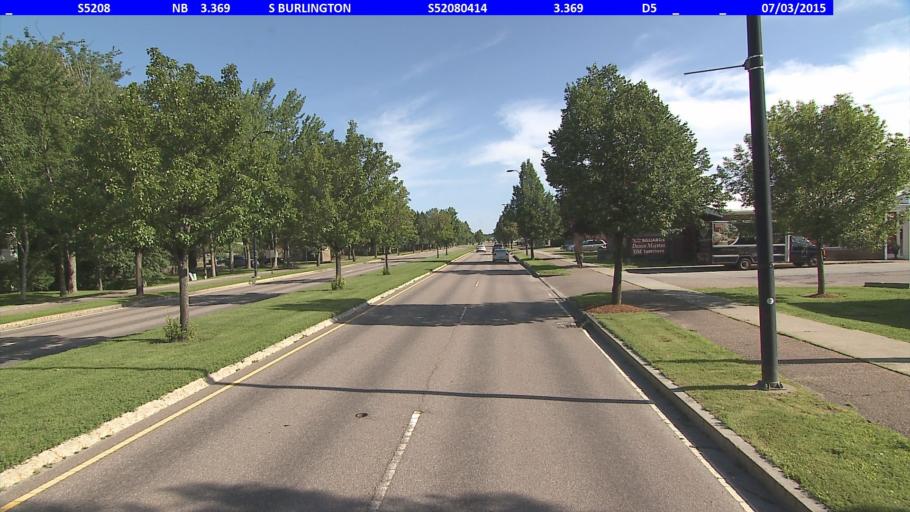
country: US
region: Vermont
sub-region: Chittenden County
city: South Burlington
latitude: 44.4587
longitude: -73.1796
